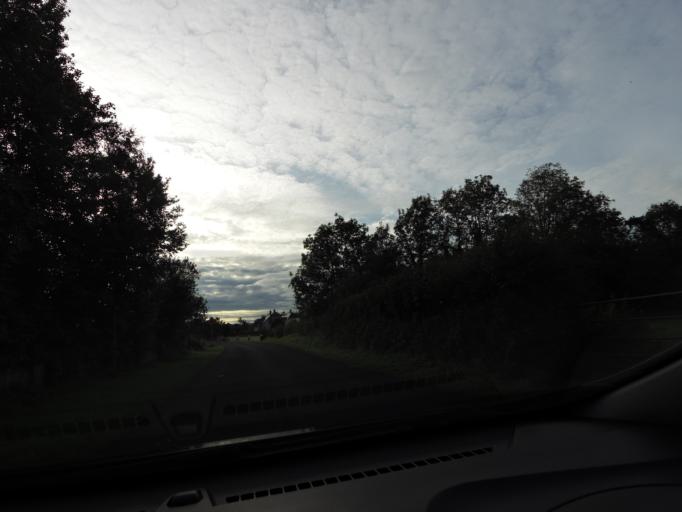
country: IE
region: Connaught
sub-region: County Galway
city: Ballinasloe
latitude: 53.3418
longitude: -8.2556
